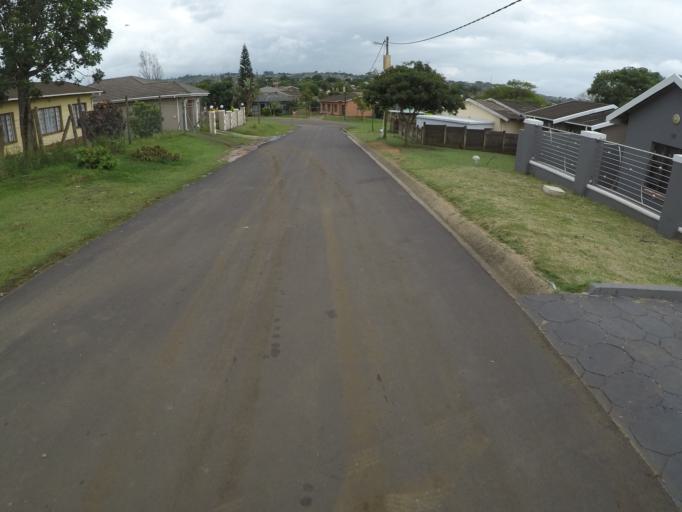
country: ZA
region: KwaZulu-Natal
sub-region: uThungulu District Municipality
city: Empangeni
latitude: -28.7833
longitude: 31.8514
